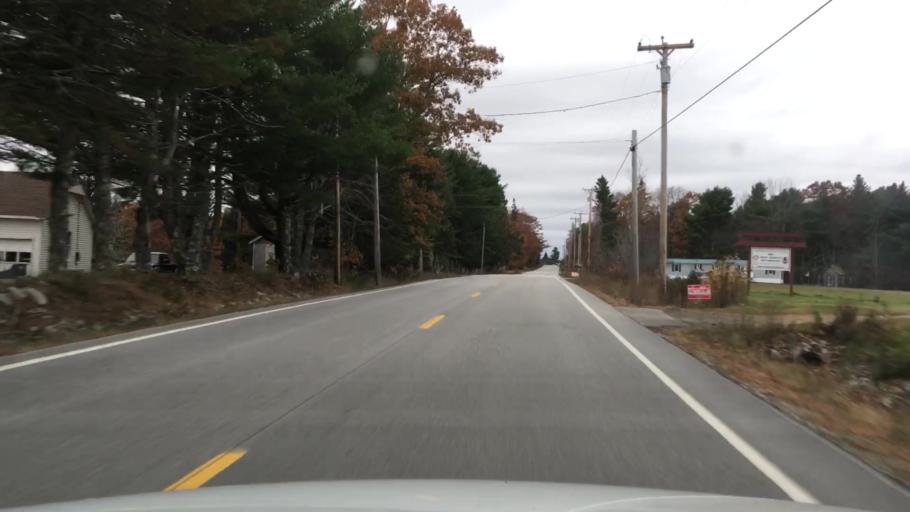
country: US
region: Maine
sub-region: Hancock County
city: Orland
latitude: 44.5420
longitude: -68.6846
